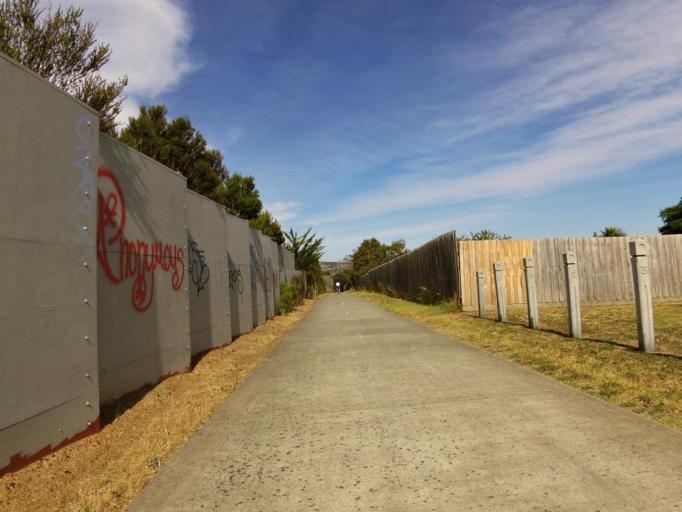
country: AU
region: Victoria
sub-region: Casey
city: Hallam
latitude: -37.9989
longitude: 145.2794
